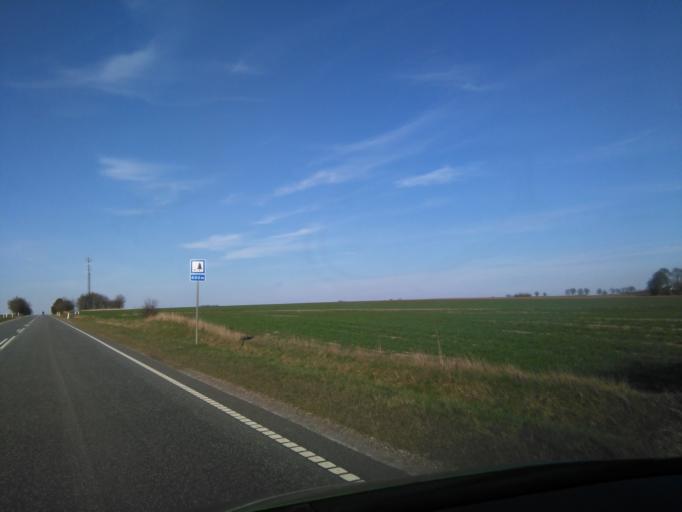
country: DK
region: Central Jutland
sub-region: Horsens Kommune
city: Braedstrup
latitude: 55.8960
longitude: 9.6483
